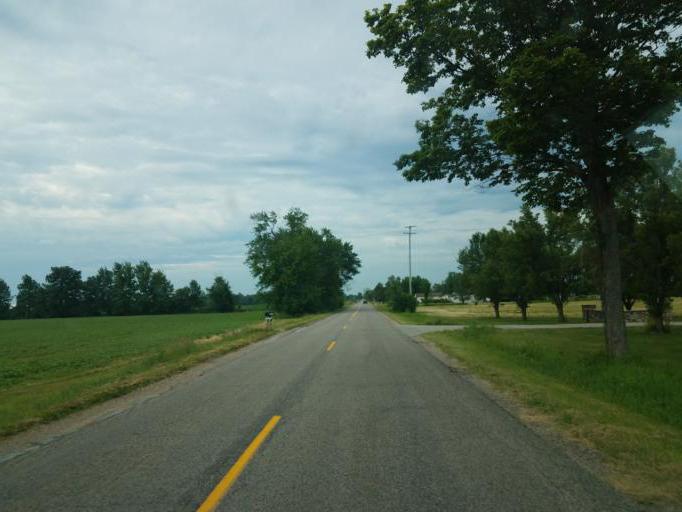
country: US
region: Michigan
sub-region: Eaton County
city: Charlotte
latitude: 42.6204
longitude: -84.8365
